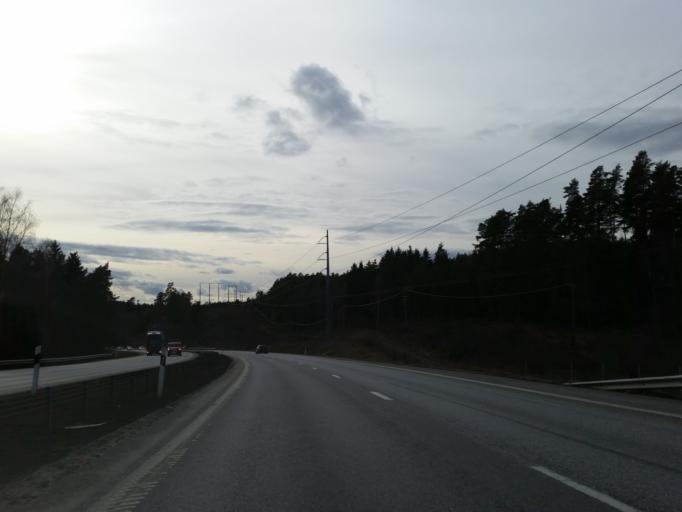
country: SE
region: OEstergoetland
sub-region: Norrkopings Kommun
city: Jursla
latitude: 58.6719
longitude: 16.2222
